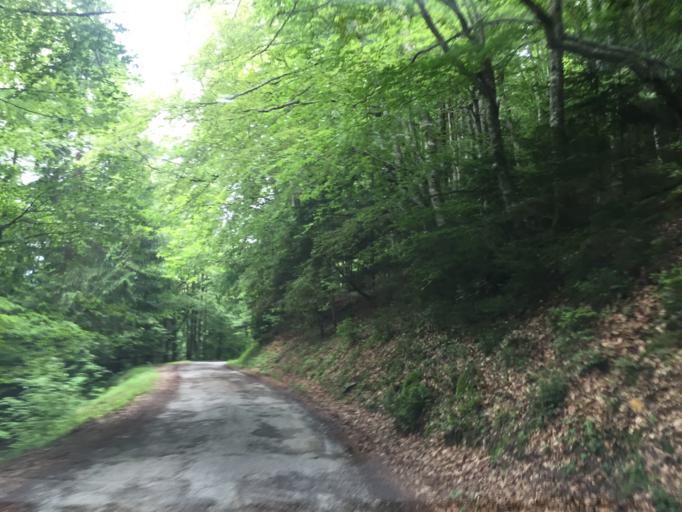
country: FR
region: Rhone-Alpes
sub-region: Departement de la Savoie
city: La Rochette
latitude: 45.4374
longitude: 6.1649
